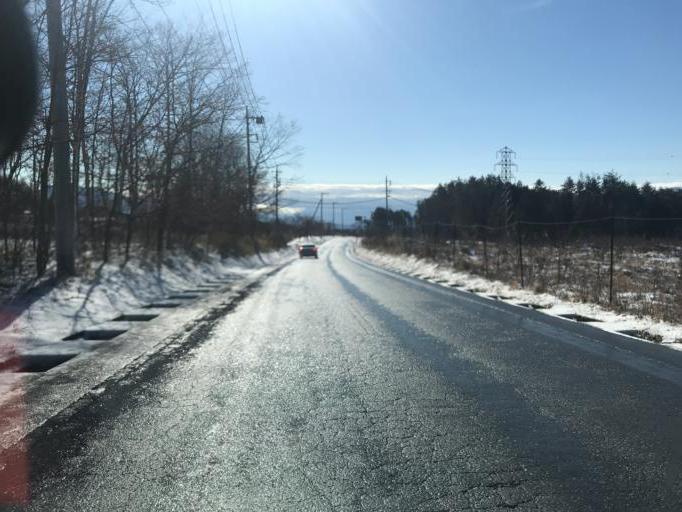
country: JP
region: Yamanashi
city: Nirasaki
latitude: 35.8654
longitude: 138.3363
